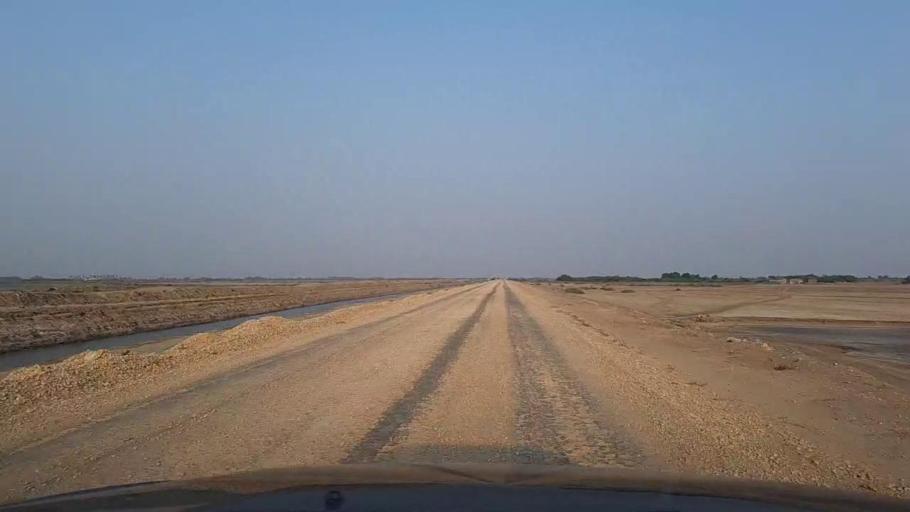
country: PK
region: Sindh
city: Mirpur Sakro
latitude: 24.4369
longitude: 67.7698
